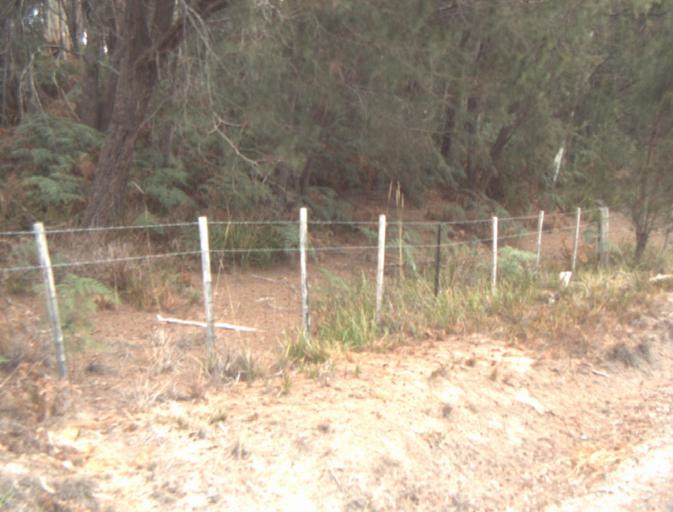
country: AU
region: Tasmania
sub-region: Launceston
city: Mayfield
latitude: -41.2830
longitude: 147.0164
